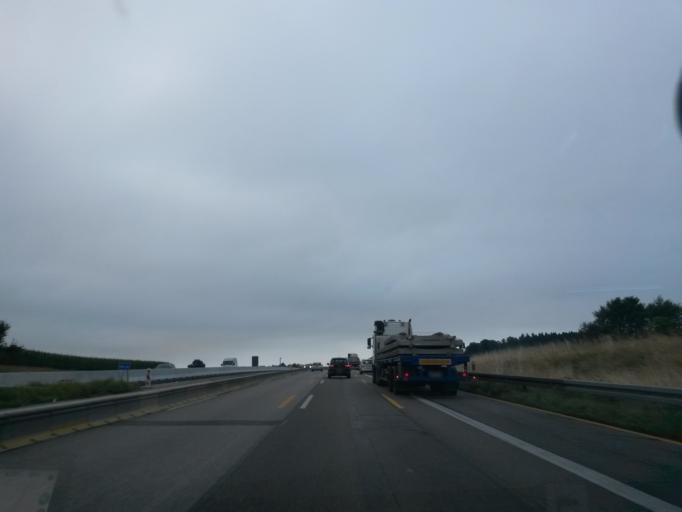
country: DE
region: Bavaria
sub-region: Upper Bavaria
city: Schweitenkirchen
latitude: 48.5452
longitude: 11.5939
